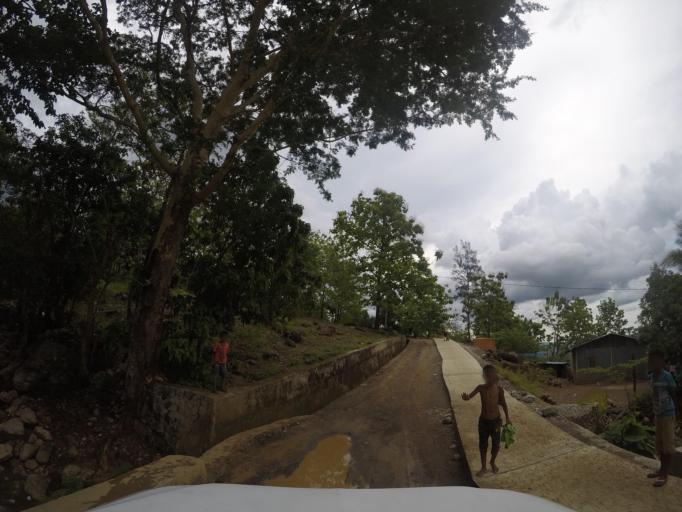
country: TL
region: Bobonaro
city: Maliana
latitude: -8.9957
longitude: 125.2148
